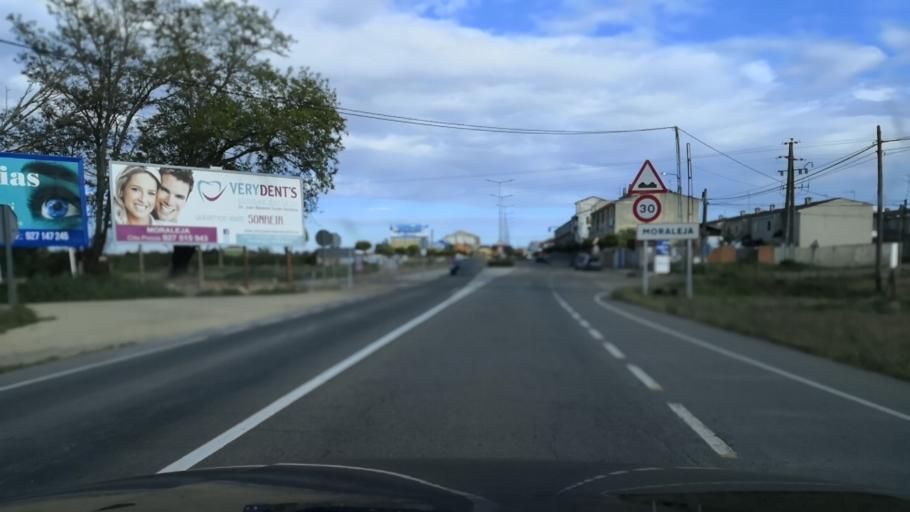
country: ES
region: Extremadura
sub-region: Provincia de Caceres
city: Moraleja
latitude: 40.0747
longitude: -6.6637
